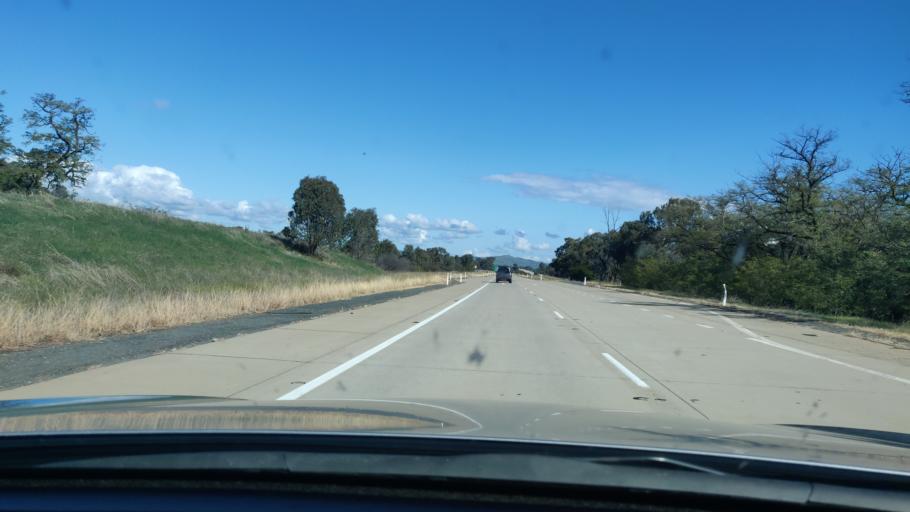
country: AU
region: New South Wales
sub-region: Greater Hume Shire
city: Holbrook
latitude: -35.6886
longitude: 147.3521
